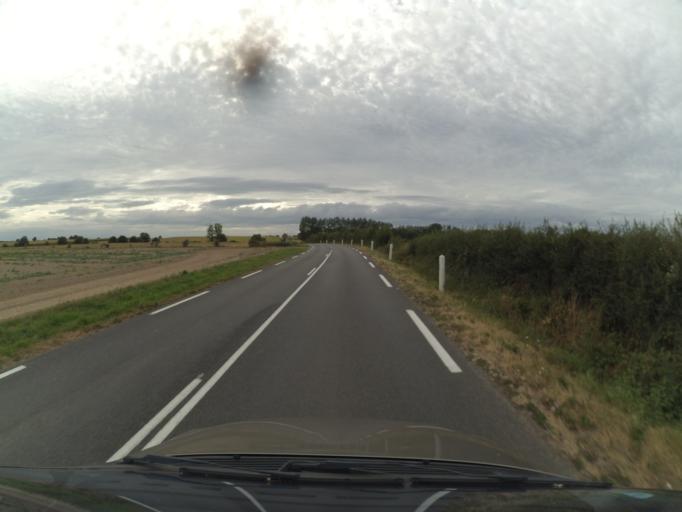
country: FR
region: Pays de la Loire
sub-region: Departement de la Vendee
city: Saint-Aubin-des-Ormeaux
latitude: 47.0187
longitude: -1.0101
